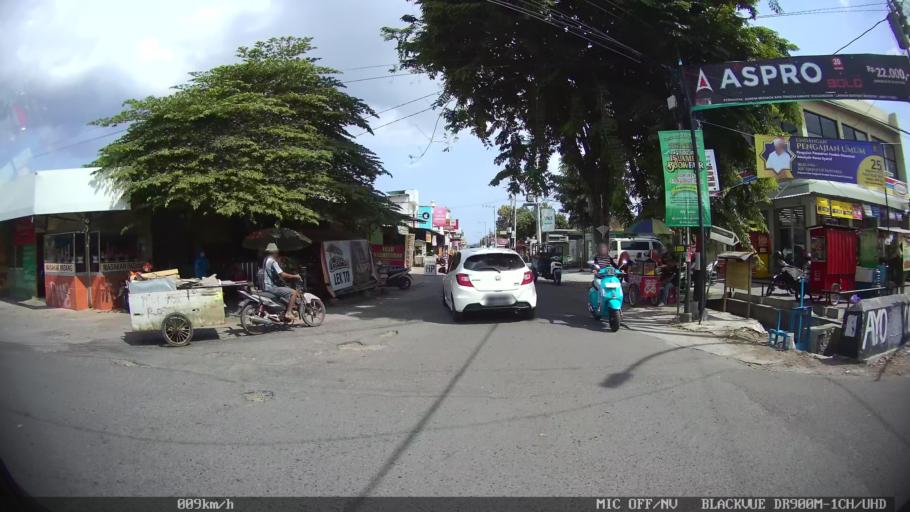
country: ID
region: Daerah Istimewa Yogyakarta
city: Kasihan
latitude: -7.8153
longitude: 110.3282
